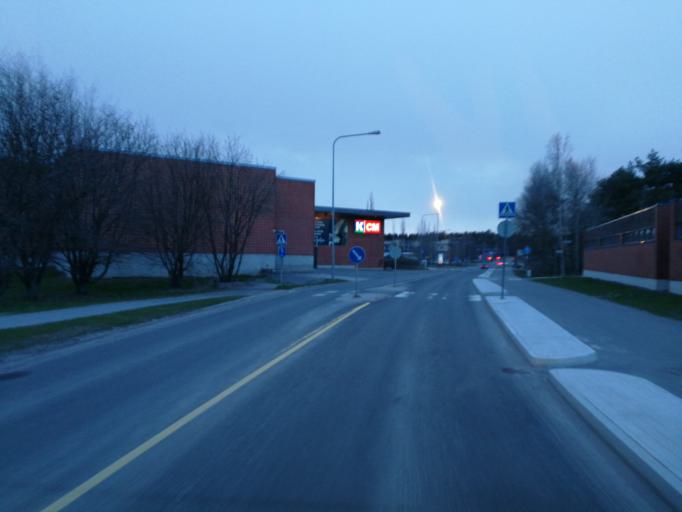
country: FI
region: Varsinais-Suomi
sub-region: Turku
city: Turku
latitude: 60.4713
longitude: 22.2349
